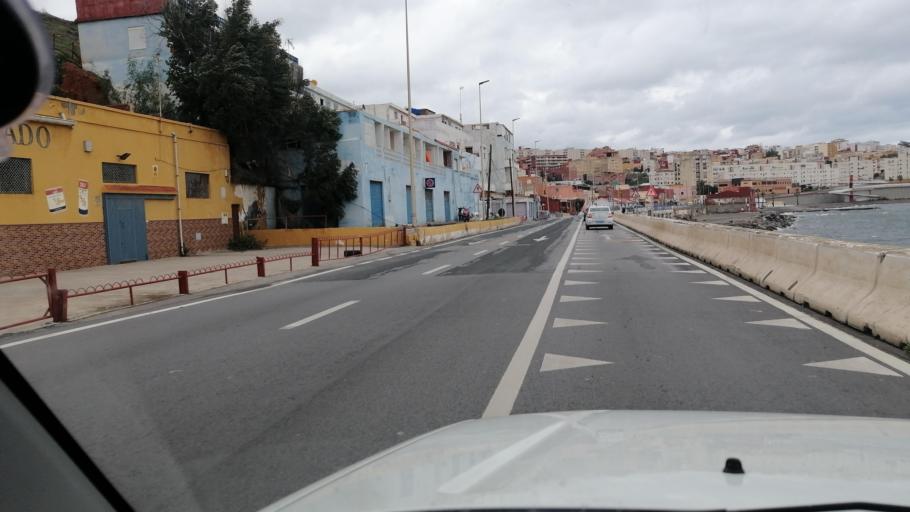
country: ES
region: Ceuta
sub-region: Ceuta
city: Ceuta
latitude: 35.8778
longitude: -5.3389
